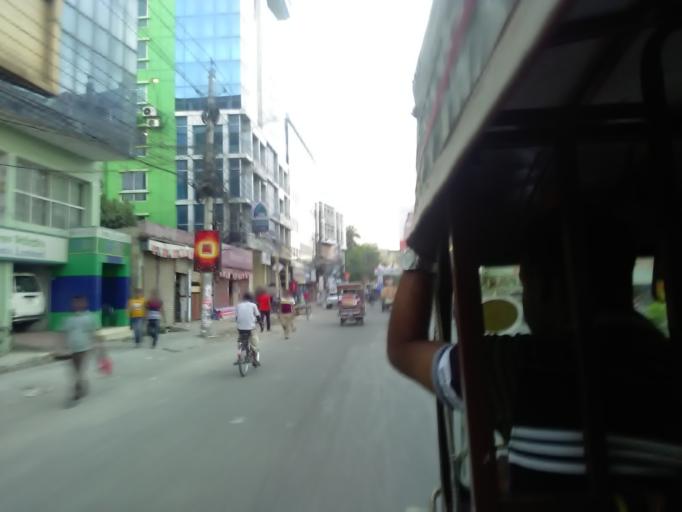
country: BD
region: Khulna
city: Khulna
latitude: 22.8200
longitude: 89.5530
